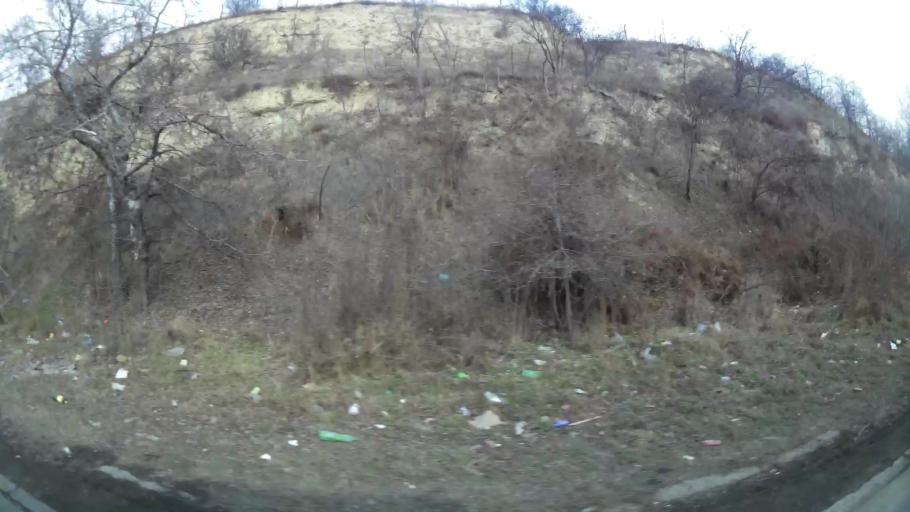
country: MK
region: Karpos
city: Skopje
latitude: 42.0131
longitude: 21.4205
